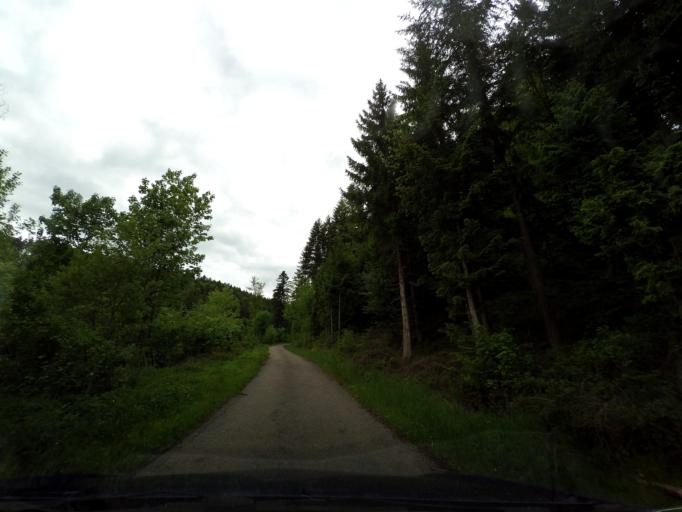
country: DE
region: Baden-Wuerttemberg
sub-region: Regierungsbezirk Stuttgart
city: Murrhardt
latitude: 49.0066
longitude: 9.5529
